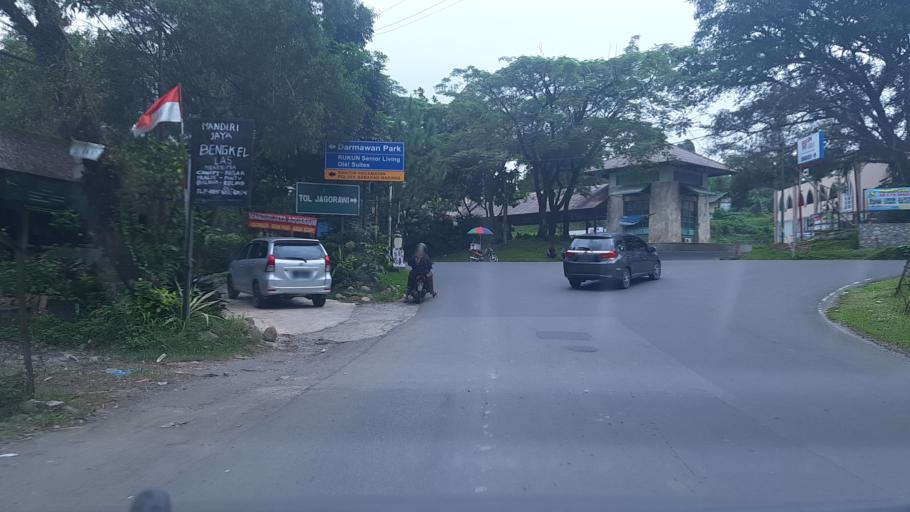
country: ID
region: West Java
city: Bogor
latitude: -6.5727
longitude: 106.8636
